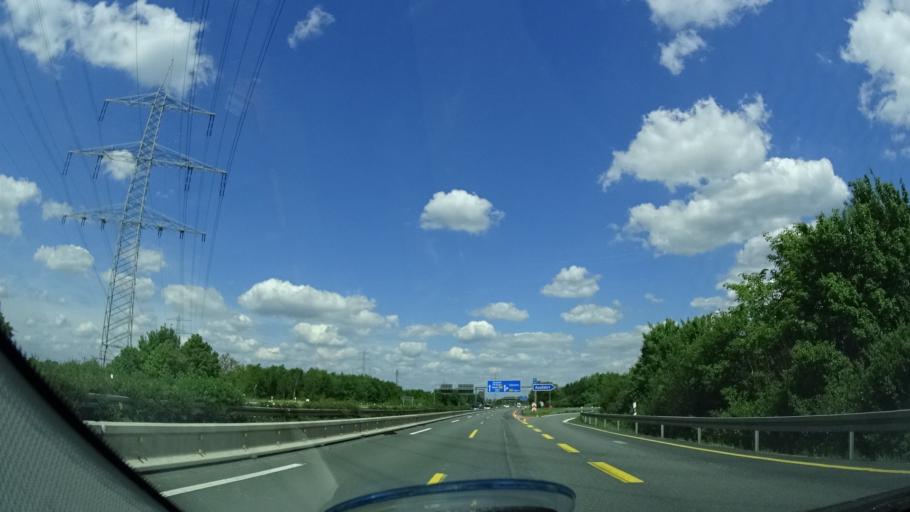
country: DE
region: North Rhine-Westphalia
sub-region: Regierungsbezirk Detmold
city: Paderborn
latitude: 51.7017
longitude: 8.7059
